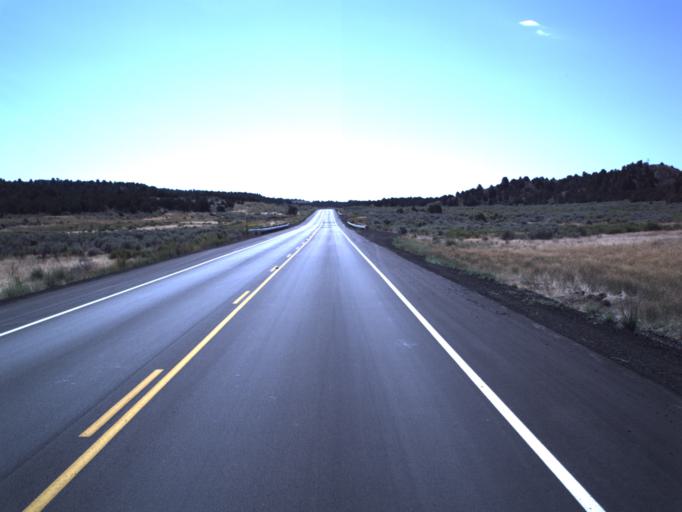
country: US
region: Utah
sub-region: Utah County
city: Eagle Mountain
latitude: 39.9959
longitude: -112.2712
